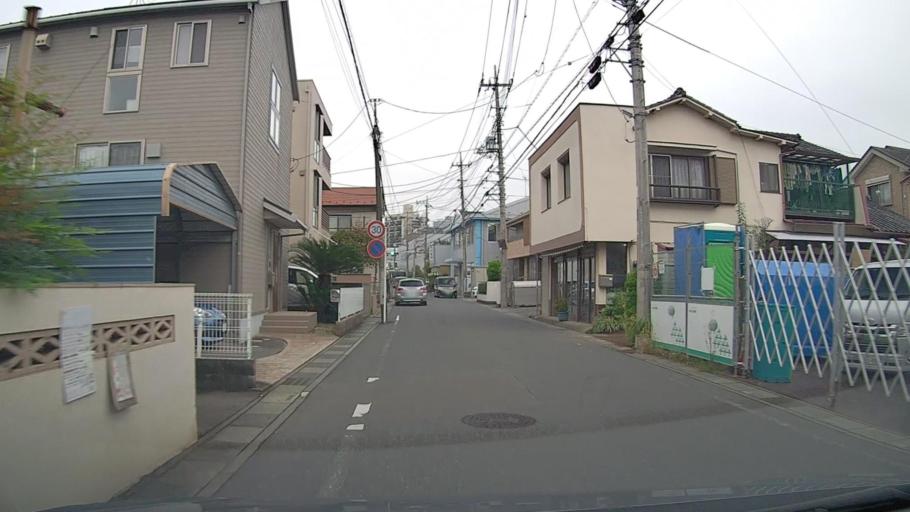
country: JP
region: Saitama
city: Tokorozawa
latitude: 35.7829
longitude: 139.4762
